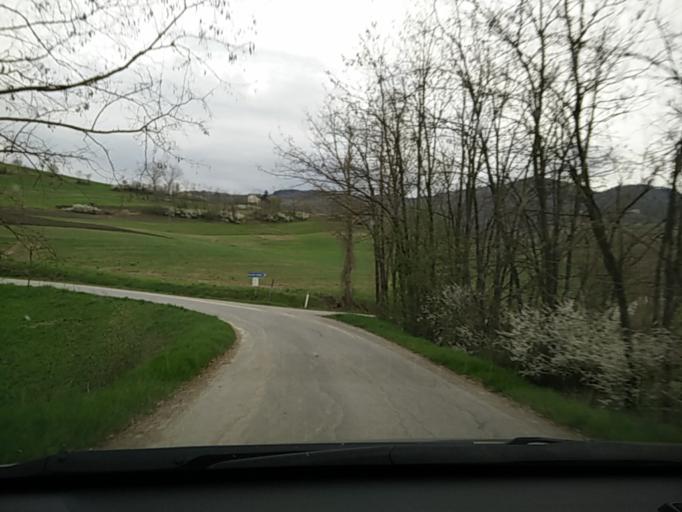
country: IT
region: Lombardy
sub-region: Provincia di Pavia
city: Susella
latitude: 44.9002
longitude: 9.1045
